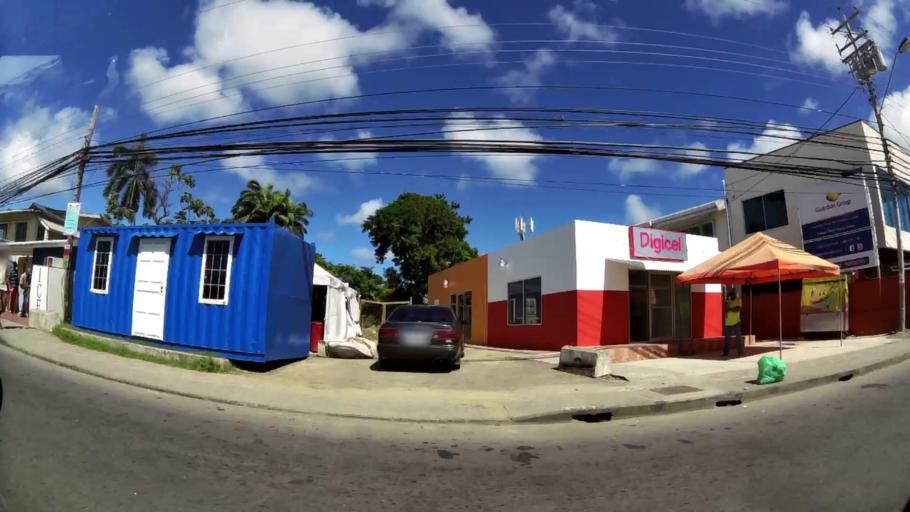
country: TT
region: Tobago
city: Scarborough
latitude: 11.1828
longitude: -60.7382
